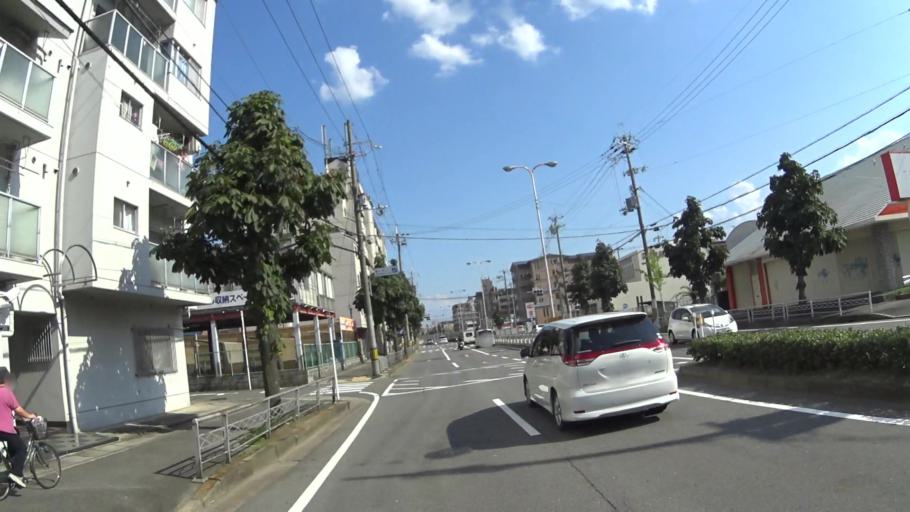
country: JP
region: Kyoto
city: Muko
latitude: 34.9753
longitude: 135.7140
